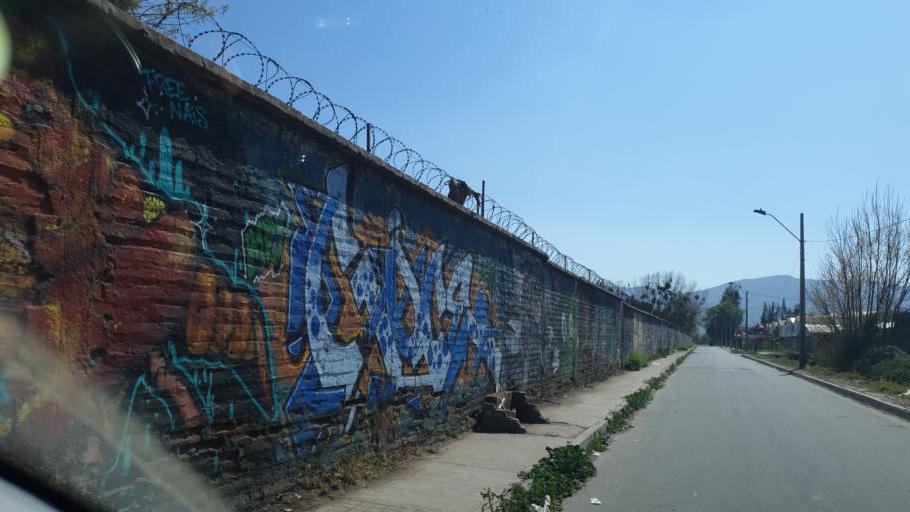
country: CL
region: Santiago Metropolitan
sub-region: Provincia de Talagante
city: Talagante
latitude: -33.6564
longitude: -70.9270
